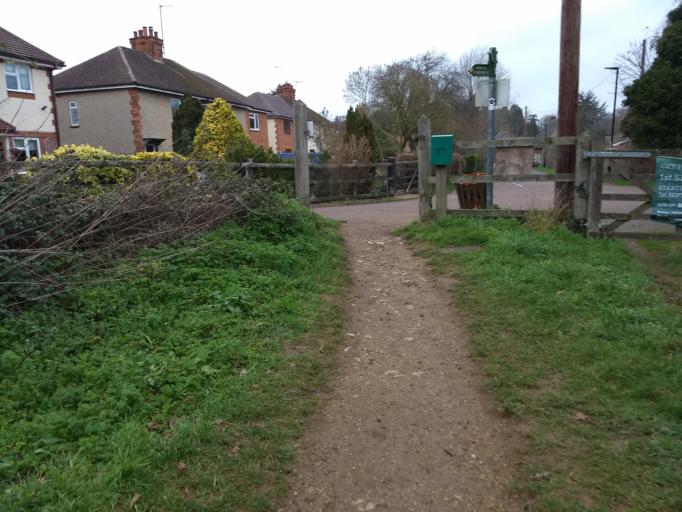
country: GB
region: England
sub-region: Bedford
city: Odell
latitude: 52.2073
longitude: -0.5905
